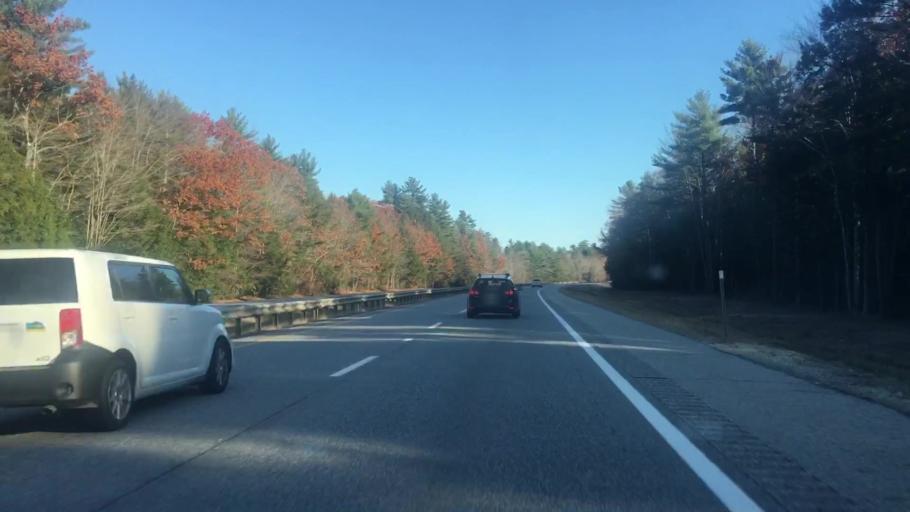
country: US
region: Maine
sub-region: Cumberland County
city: New Gloucester
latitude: 43.9678
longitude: -70.3246
